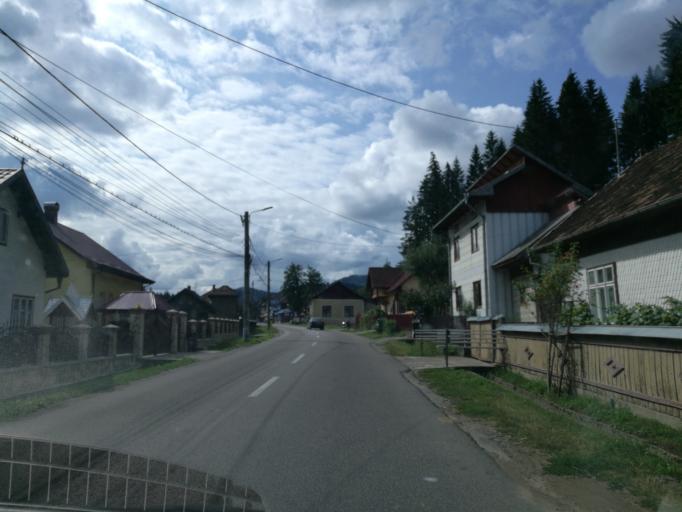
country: RO
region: Suceava
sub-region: Oras Gura Humorului
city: Gura Humorului
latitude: 47.5288
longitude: 25.8637
